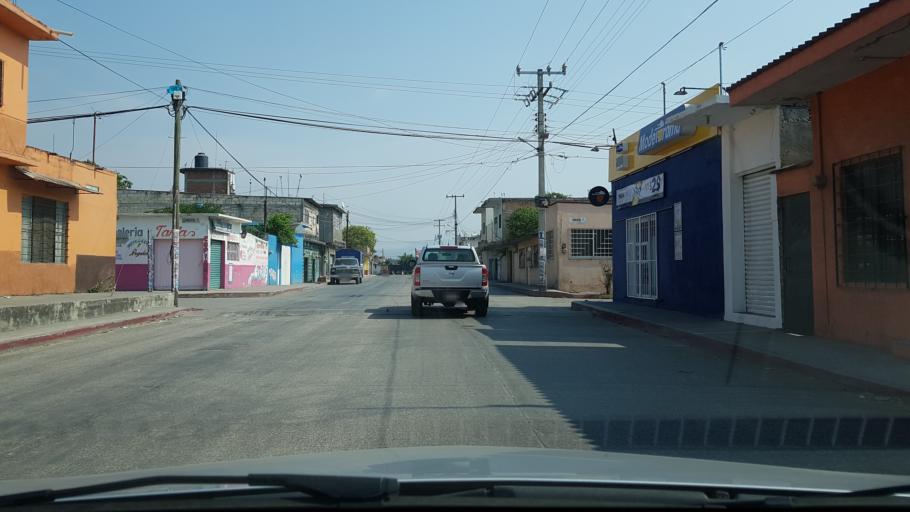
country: MX
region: Morelos
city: Zacatepec
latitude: 18.6619
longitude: -99.1860
